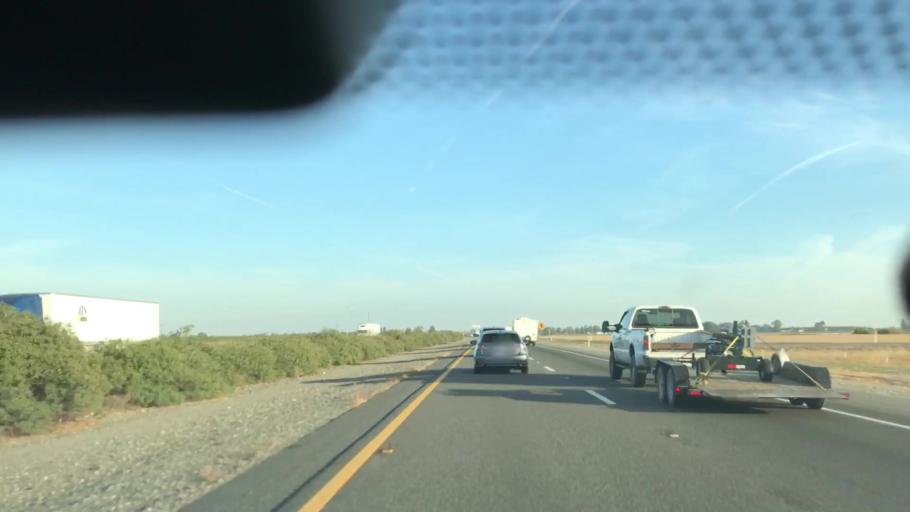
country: US
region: California
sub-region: Glenn County
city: Orland
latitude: 39.6839
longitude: -122.2064
